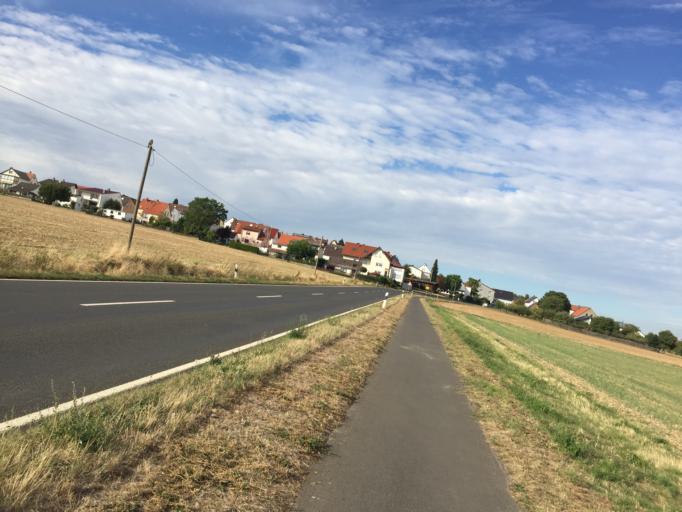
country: DE
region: Hesse
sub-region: Regierungsbezirk Giessen
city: Langgons
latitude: 50.5028
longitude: 8.7290
